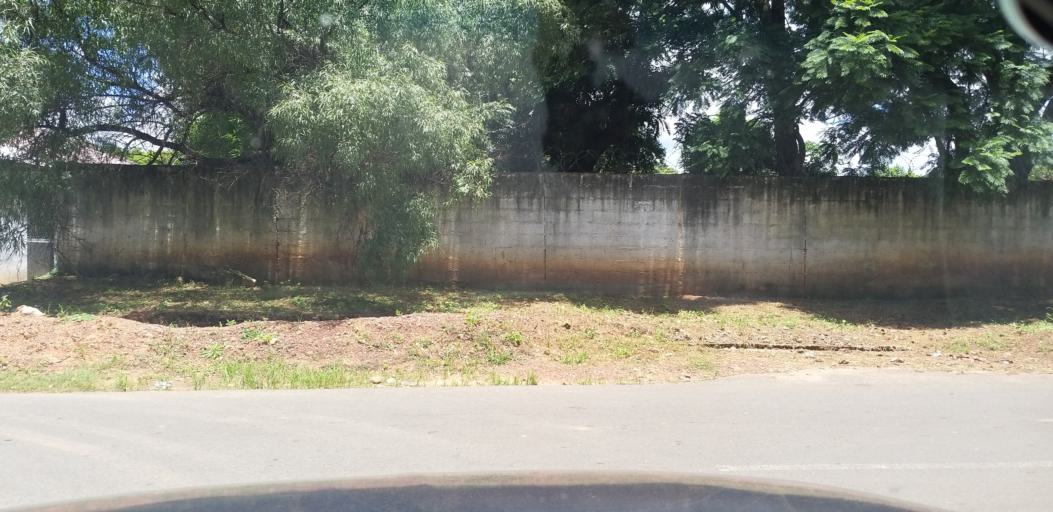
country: ZM
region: Lusaka
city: Lusaka
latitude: -15.4182
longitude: 28.3023
